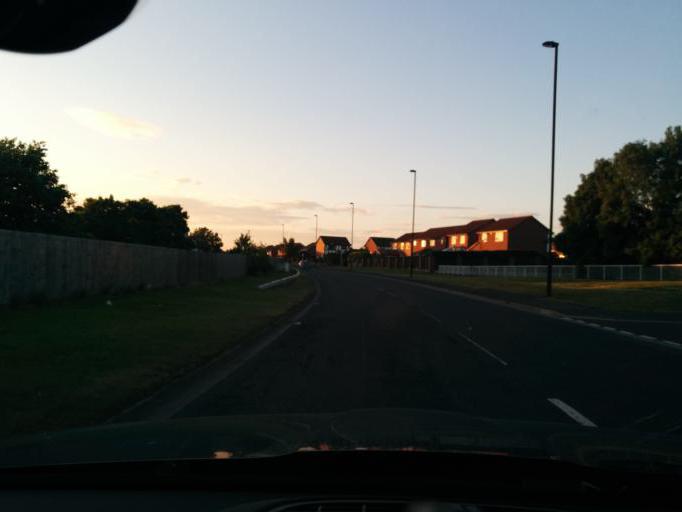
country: GB
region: England
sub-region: Northumberland
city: Seghill
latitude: 55.0397
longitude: -1.5643
